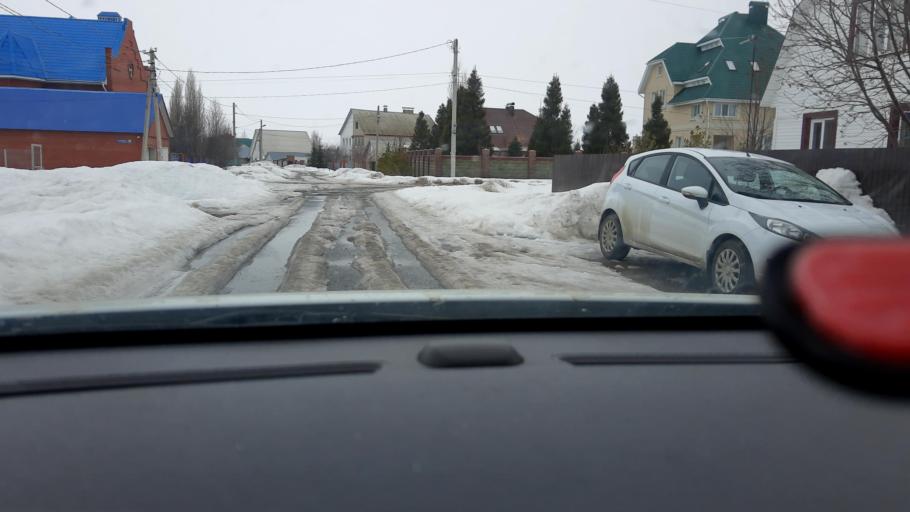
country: RU
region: Bashkortostan
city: Avdon
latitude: 54.4938
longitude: 55.8753
